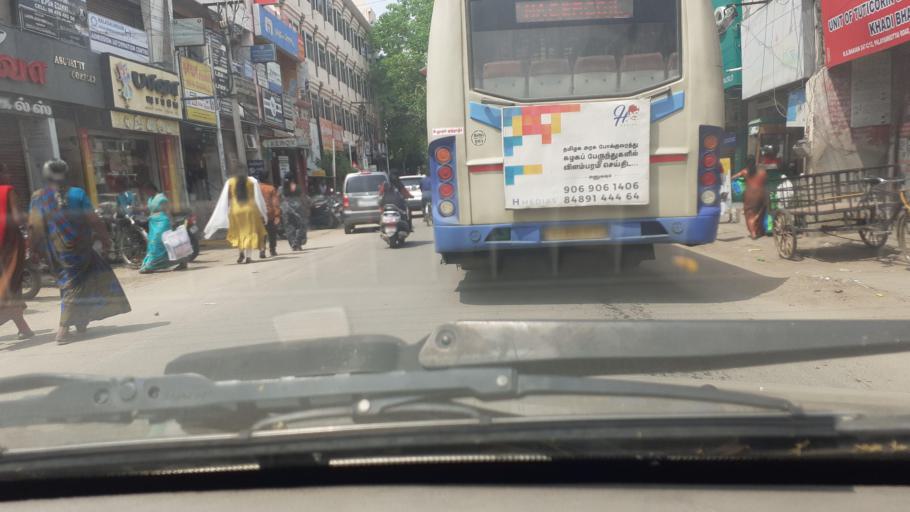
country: IN
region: Tamil Nadu
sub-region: Thoothukkudi
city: Korampallam
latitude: 8.8025
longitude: 78.1397
